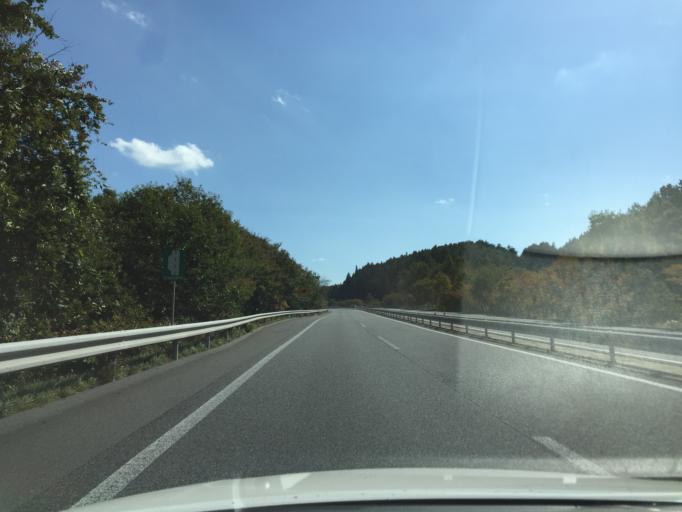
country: JP
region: Fukushima
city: Funehikimachi-funehiki
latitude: 37.2282
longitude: 140.6835
